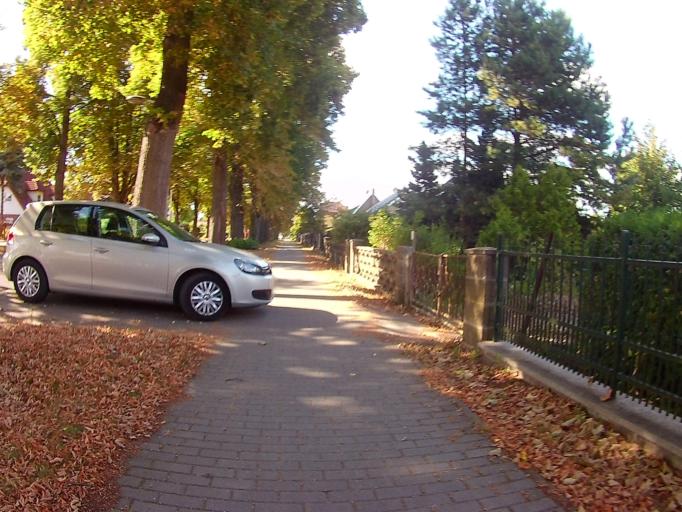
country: DE
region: Brandenburg
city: Zeuthen
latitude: 52.3678
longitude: 13.6070
